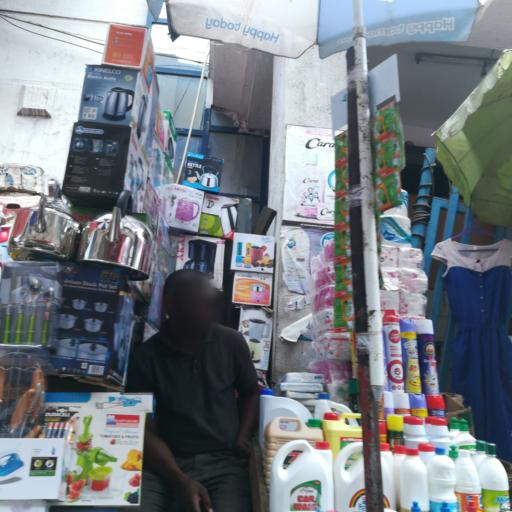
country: NG
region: Lagos
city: Lagos
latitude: 6.4567
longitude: 3.3829
